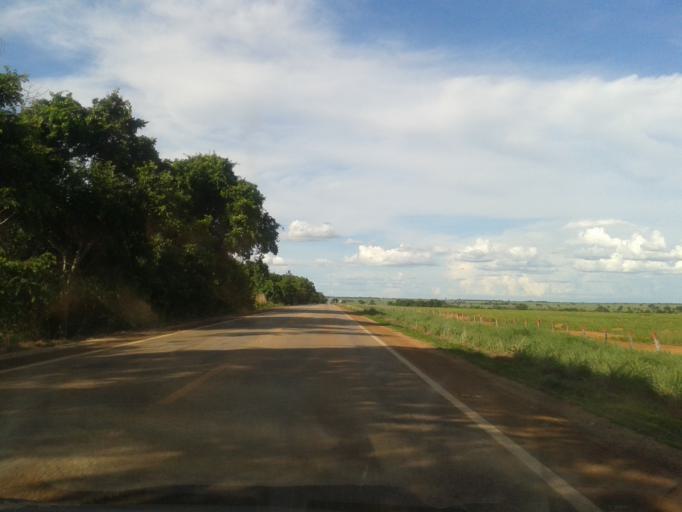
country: BR
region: Goias
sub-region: Mozarlandia
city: Mozarlandia
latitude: -14.3870
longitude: -50.4372
